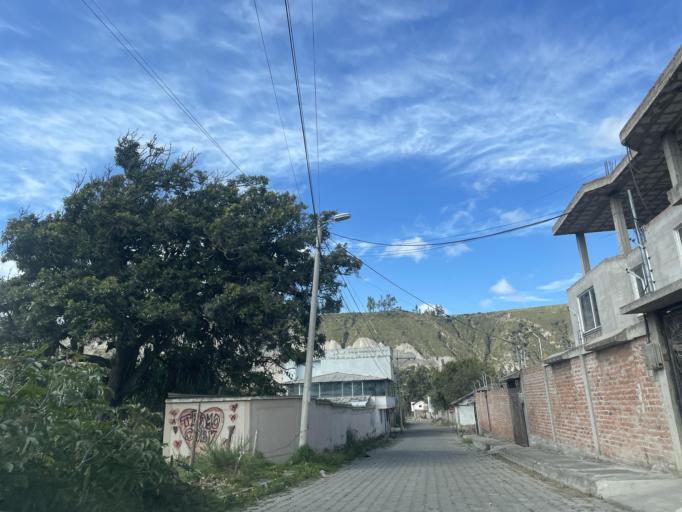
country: EC
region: Chimborazo
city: Guano
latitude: -1.6073
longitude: -78.6318
